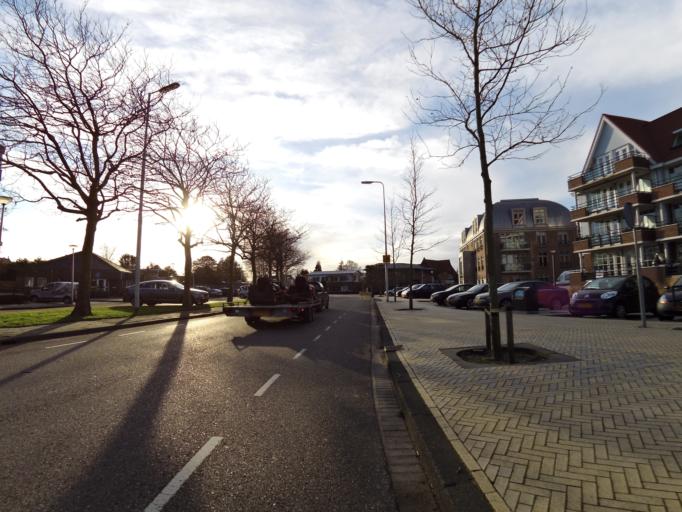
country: NL
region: South Holland
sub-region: Gemeente Brielle
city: Brielle
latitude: 51.9142
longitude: 4.1042
